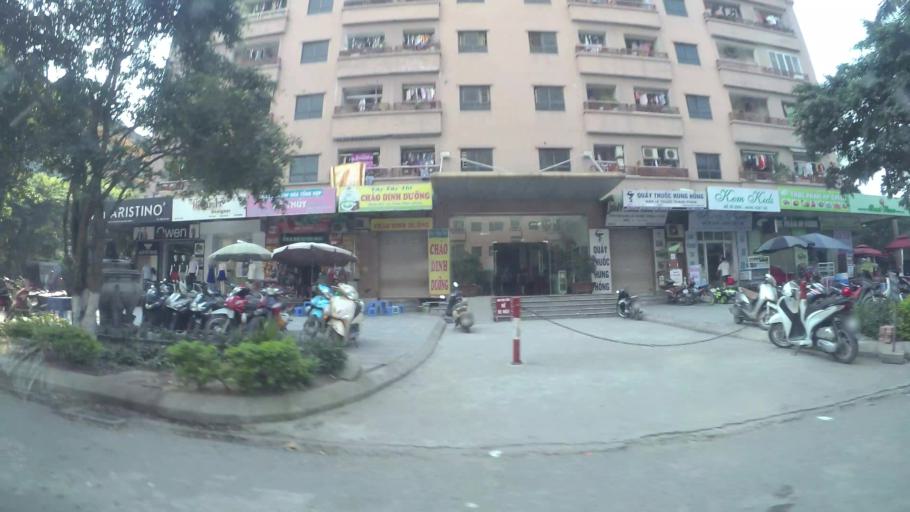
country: VN
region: Ha Noi
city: Ha Dong
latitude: 20.9565
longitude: 105.8077
